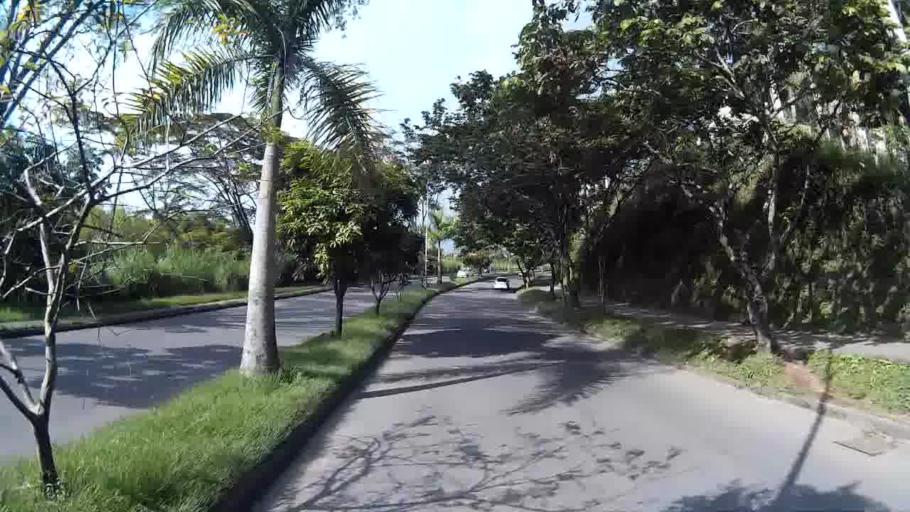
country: CO
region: Quindio
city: Armenia
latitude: 4.5432
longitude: -75.6603
